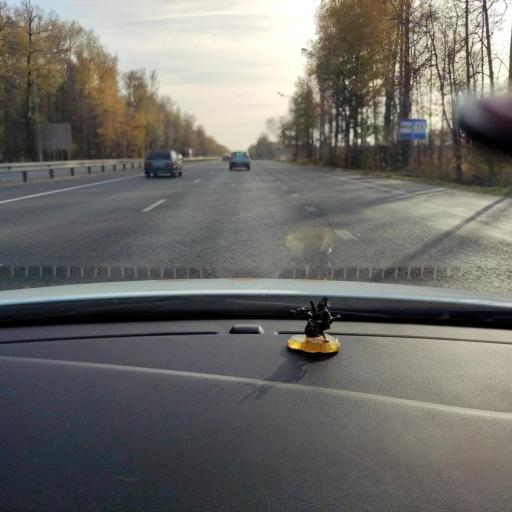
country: RU
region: Tatarstan
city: Osinovo
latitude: 55.8514
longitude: 48.8534
